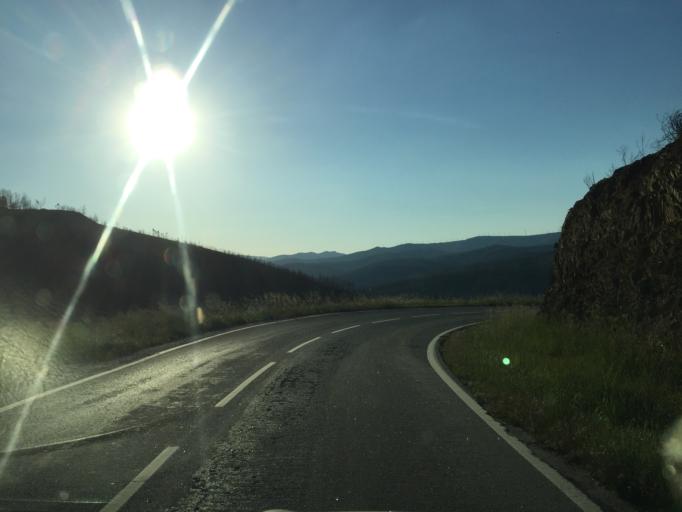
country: PT
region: Coimbra
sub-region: Pampilhosa da Serra
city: Pampilhosa da Serra
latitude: 40.0308
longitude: -7.9610
